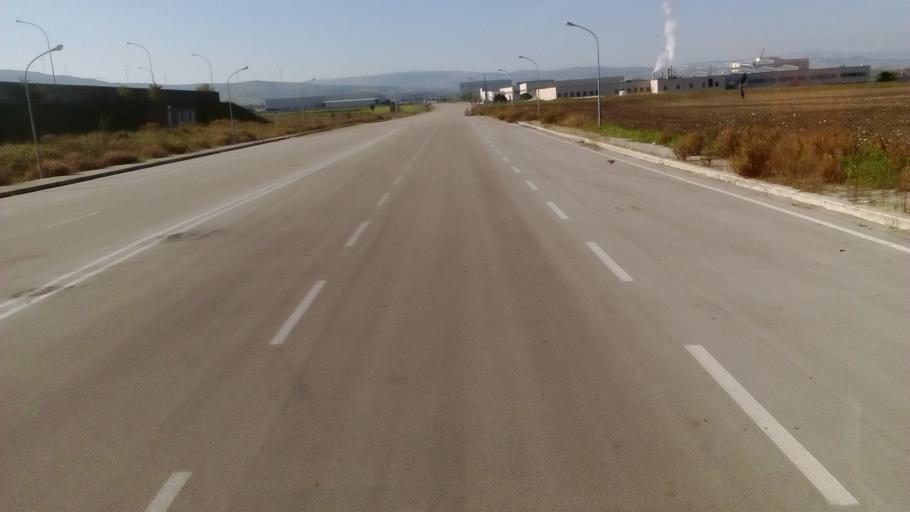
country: IT
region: Basilicate
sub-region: Provincia di Potenza
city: Melfi
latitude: 41.0778
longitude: 15.6705
